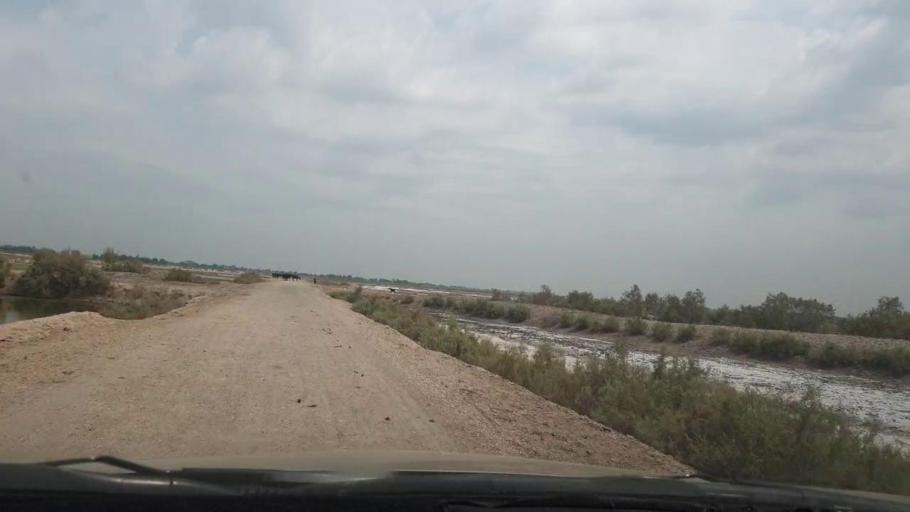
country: PK
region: Sindh
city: Ratodero
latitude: 27.7053
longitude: 68.2289
